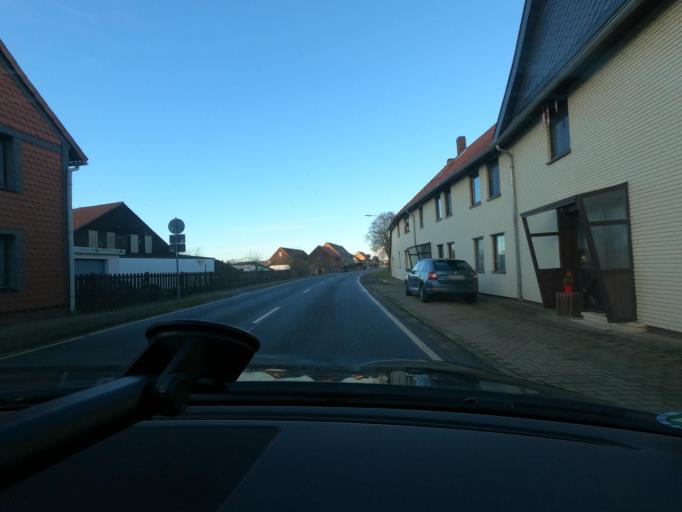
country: DE
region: Lower Saxony
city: Rhumspringe
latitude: 51.6102
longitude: 10.3226
